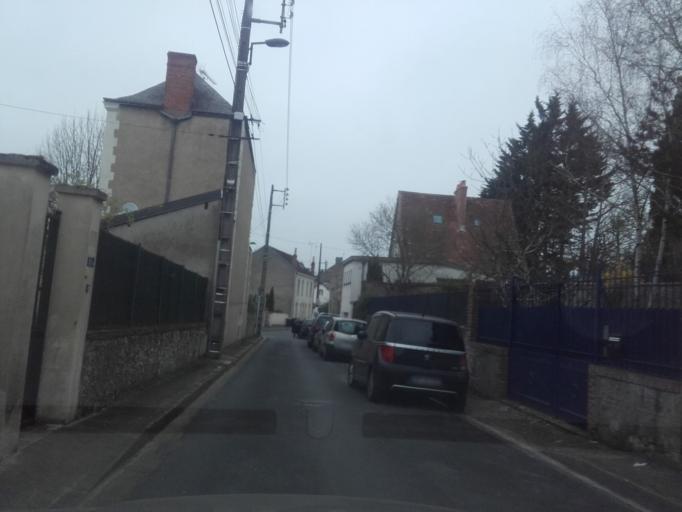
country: FR
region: Centre
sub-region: Departement d'Indre-et-Loire
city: Saint-Cyr-sur-Loire
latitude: 47.4056
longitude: 0.6799
